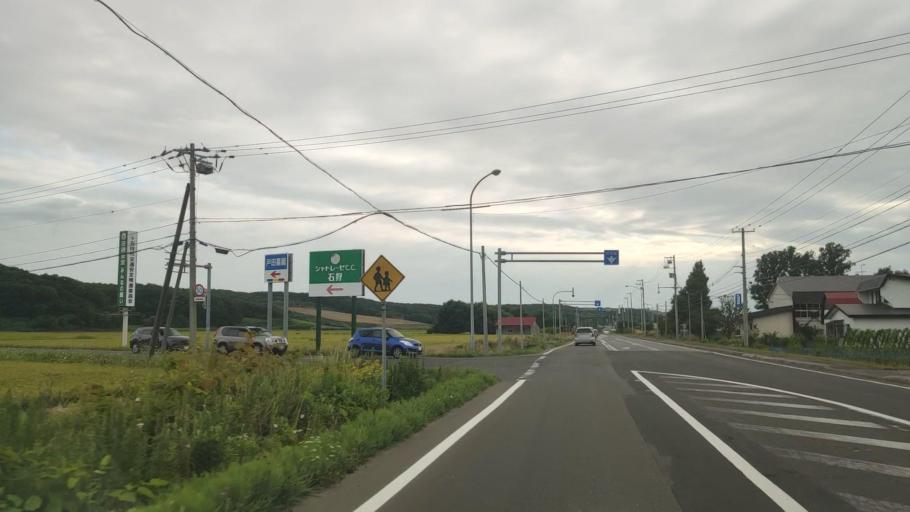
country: JP
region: Hokkaido
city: Ishikari
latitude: 43.3189
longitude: 141.4286
